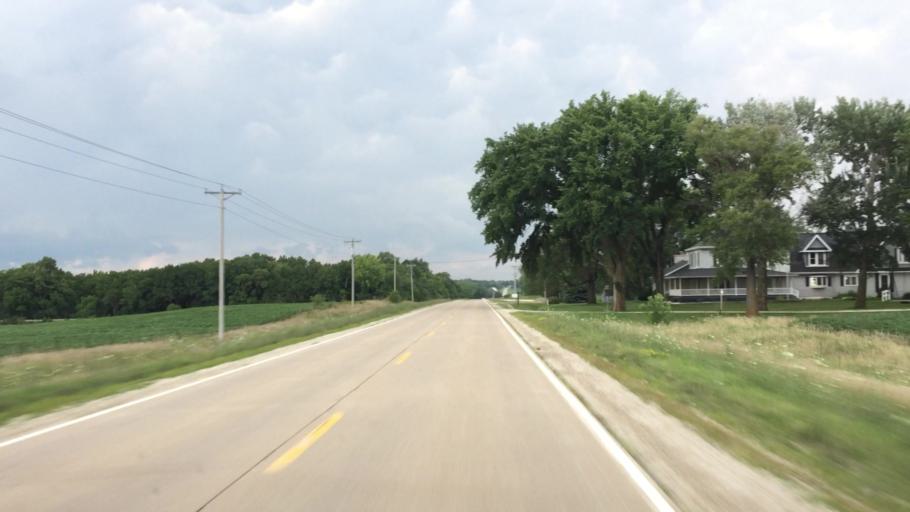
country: US
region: Iowa
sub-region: Lee County
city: Fort Madison
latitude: 40.7084
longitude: -91.3299
